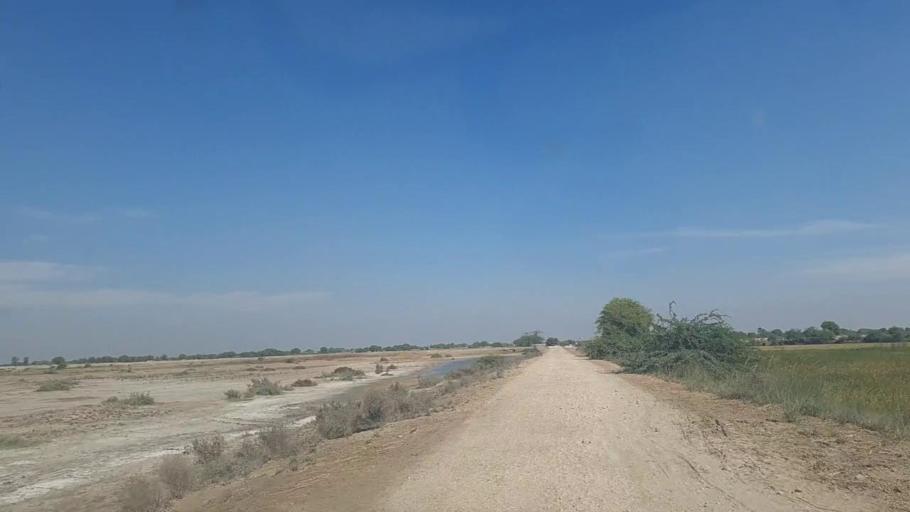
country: PK
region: Sindh
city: Mirpur Batoro
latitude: 24.7056
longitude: 68.2409
